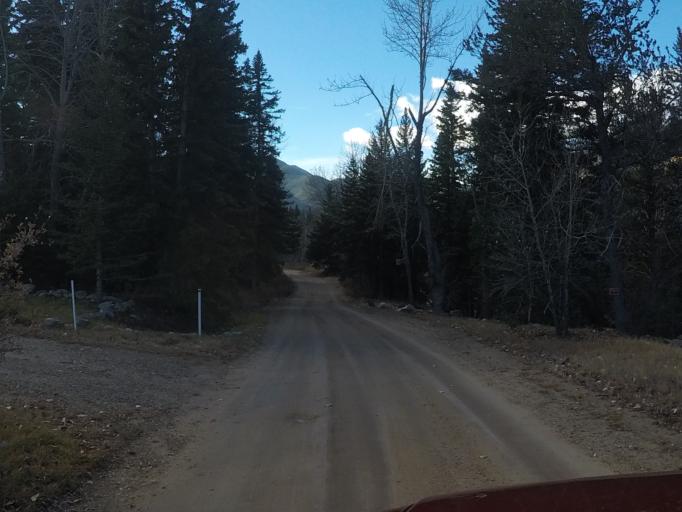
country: US
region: Montana
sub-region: Carbon County
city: Red Lodge
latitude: 45.1173
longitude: -109.2990
